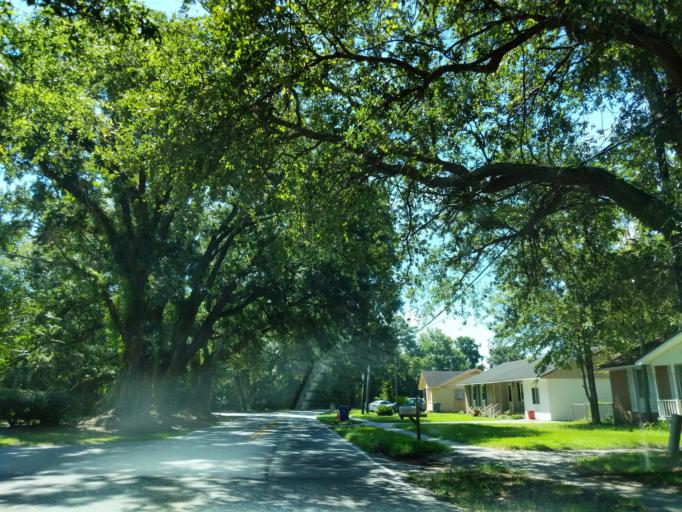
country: US
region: South Carolina
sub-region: Charleston County
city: Folly Beach
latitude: 32.7107
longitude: -79.9580
